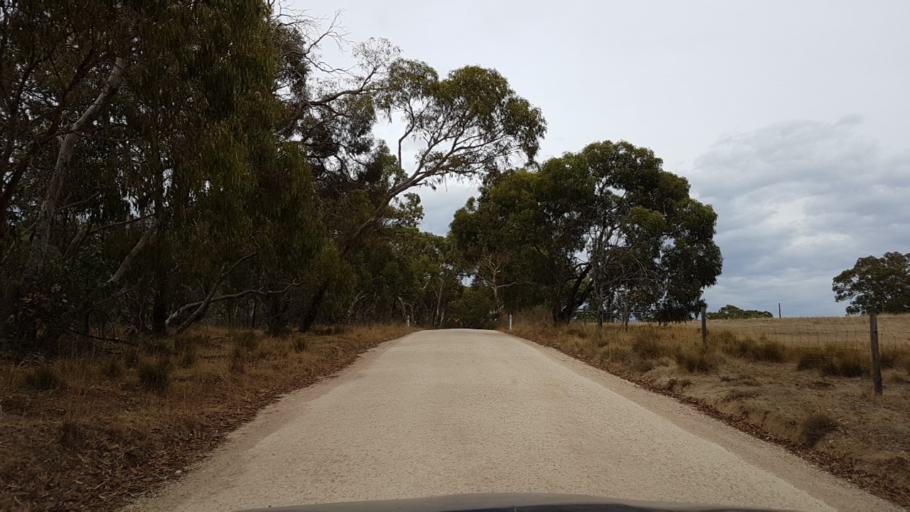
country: AU
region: South Australia
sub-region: Adelaide Hills
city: Birdwood
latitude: -34.7865
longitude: 138.9763
